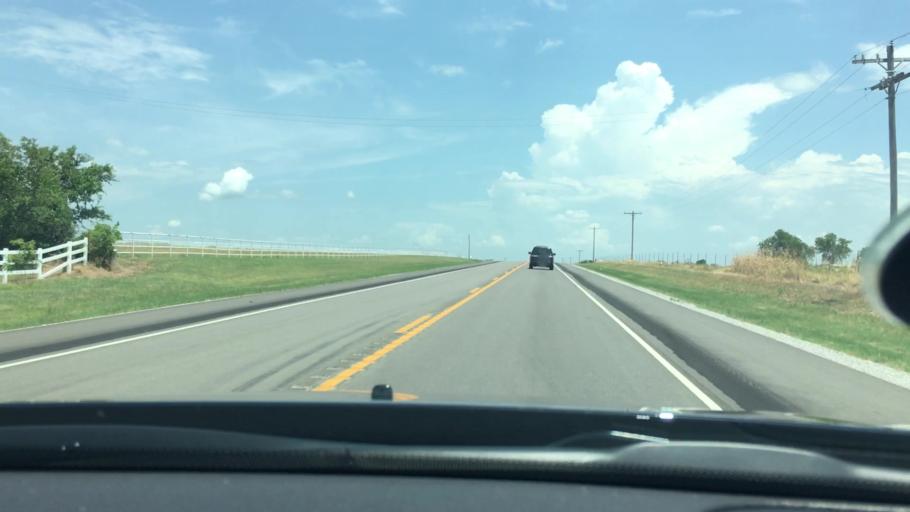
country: US
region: Oklahoma
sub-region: Love County
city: Marietta
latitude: 33.9404
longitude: -97.1961
